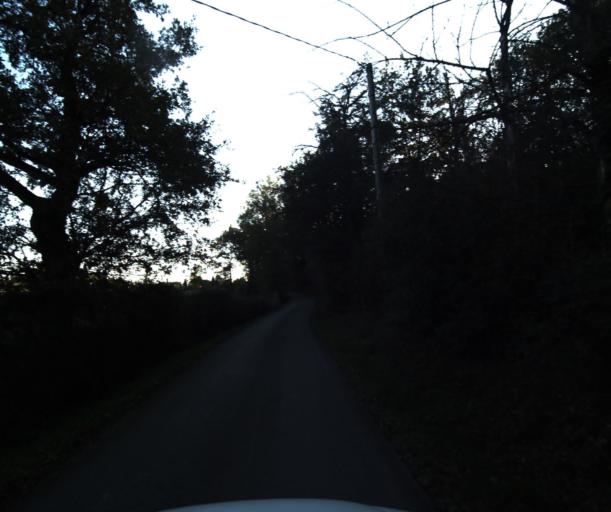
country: FR
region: Midi-Pyrenees
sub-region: Departement de la Haute-Garonne
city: Colomiers
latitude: 43.6263
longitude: 1.3428
